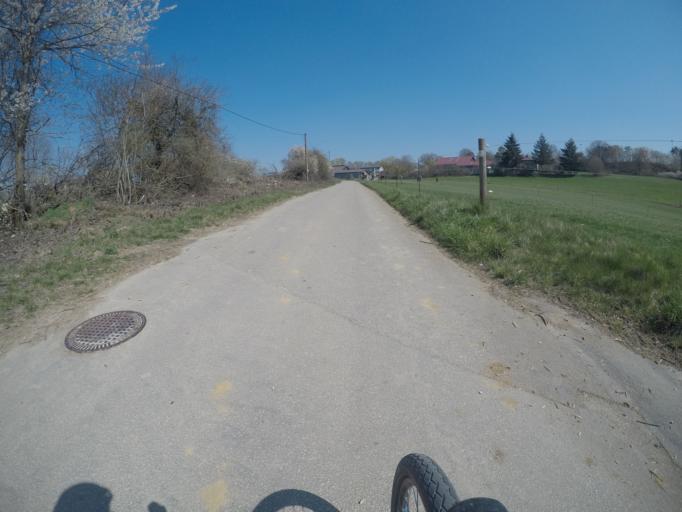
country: DE
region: Baden-Wuerttemberg
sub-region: Regierungsbezirk Stuttgart
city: Weil der Stadt
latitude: 48.7305
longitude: 8.9011
